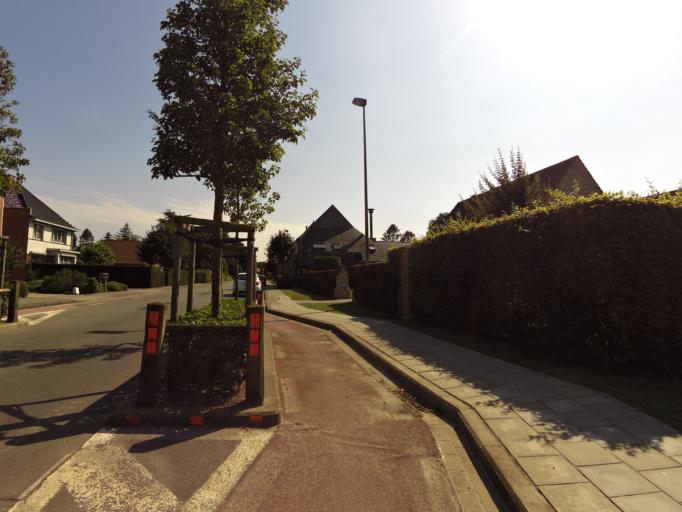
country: BE
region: Flanders
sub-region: Provincie West-Vlaanderen
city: Zedelgem
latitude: 51.1874
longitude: 3.1424
